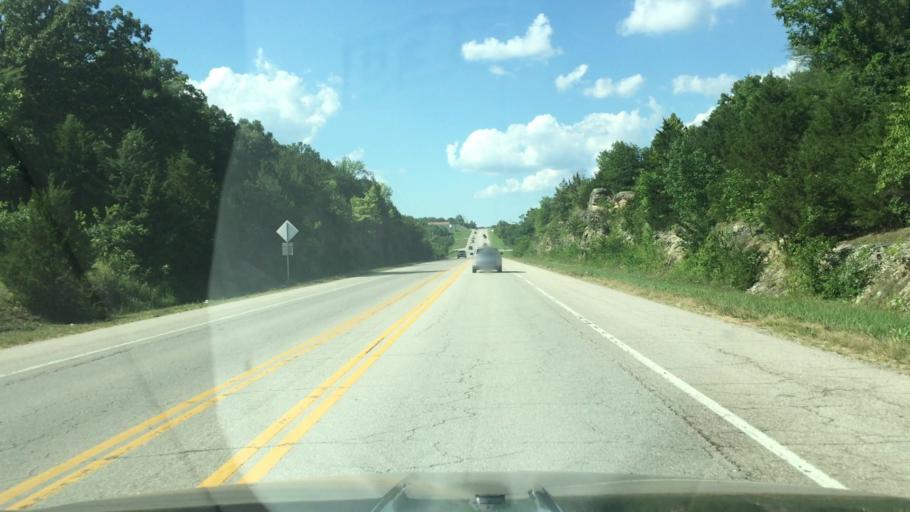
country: US
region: Missouri
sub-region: Miller County
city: Eldon
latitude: 38.3193
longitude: -92.5880
